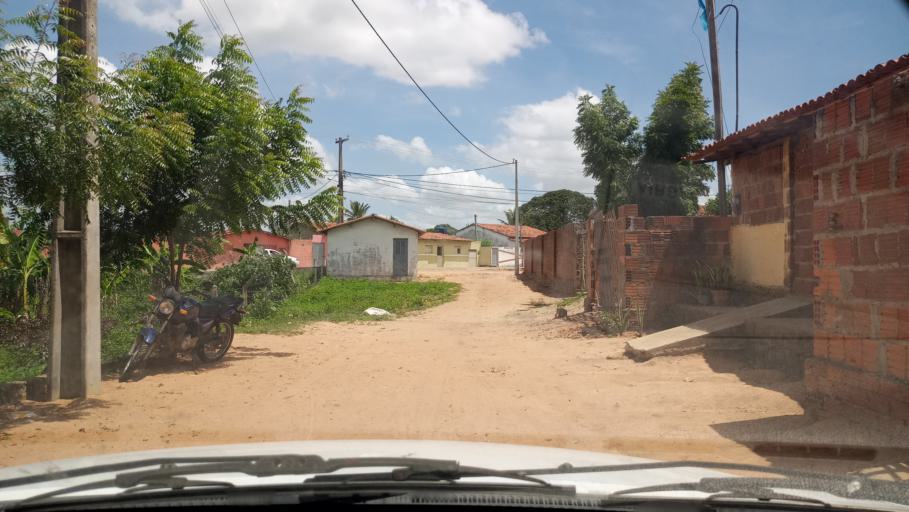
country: BR
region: Rio Grande do Norte
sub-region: Brejinho
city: Brejinho
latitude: -6.2649
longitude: -35.3740
